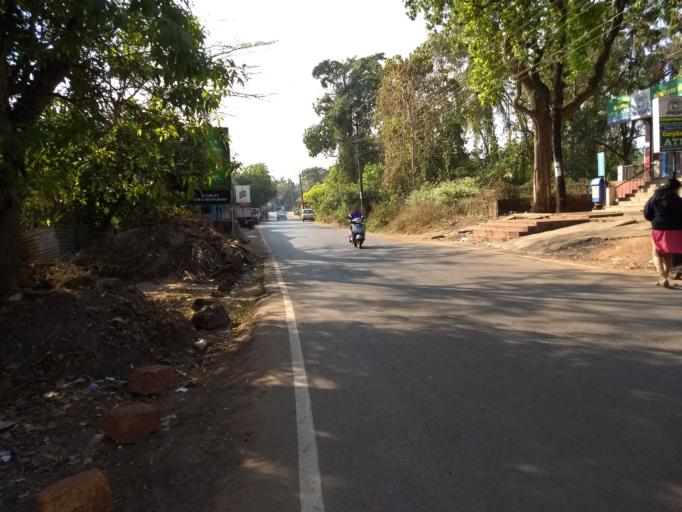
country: IN
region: Goa
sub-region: North Goa
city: Vagator
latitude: 15.5970
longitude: 73.7444
